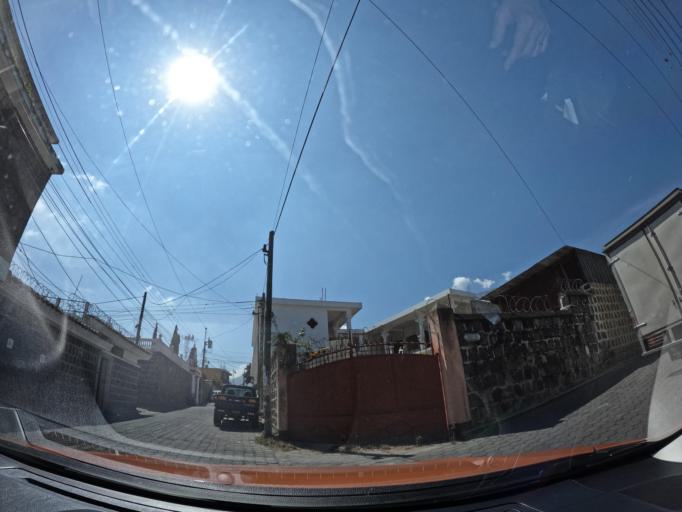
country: GT
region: Solola
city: San Lucas Toliman
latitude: 14.6349
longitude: -91.1415
